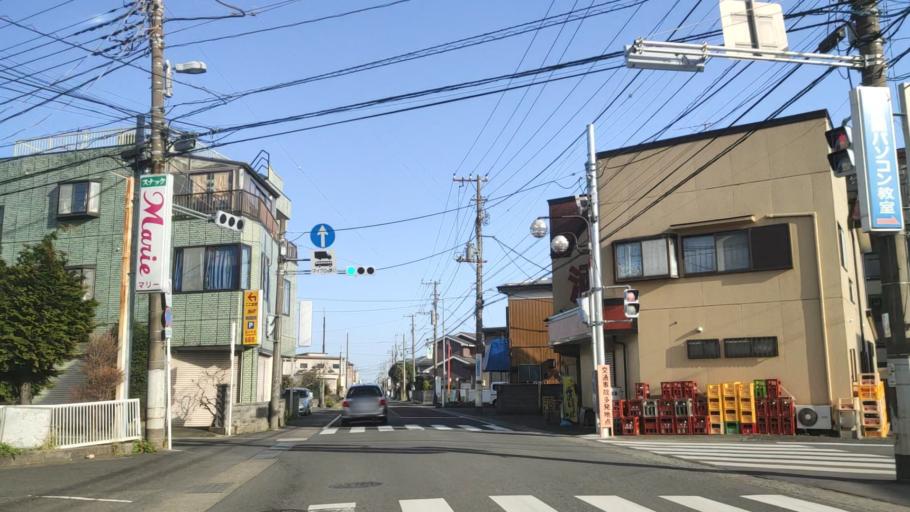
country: JP
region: Kanagawa
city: Zama
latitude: 35.5037
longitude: 139.3521
